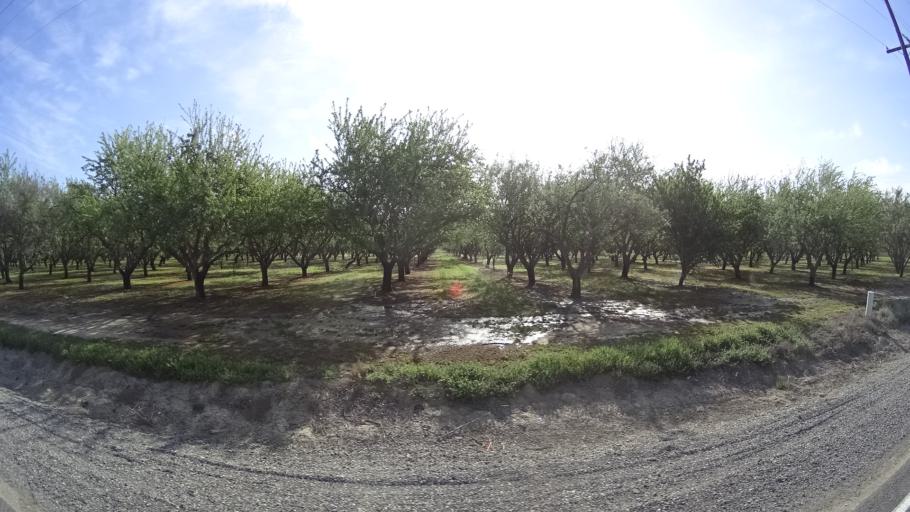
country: US
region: California
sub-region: Glenn County
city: Hamilton City
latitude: 39.5932
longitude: -122.0076
